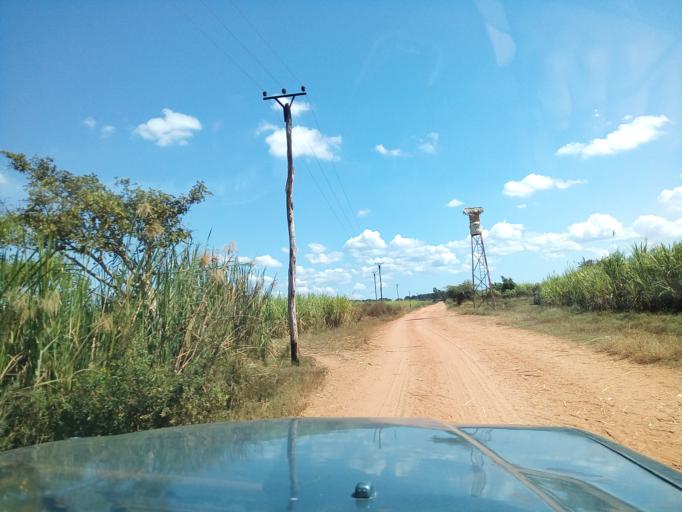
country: MG
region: Boeny
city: Mahajanga
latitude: -15.9531
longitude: 45.9090
